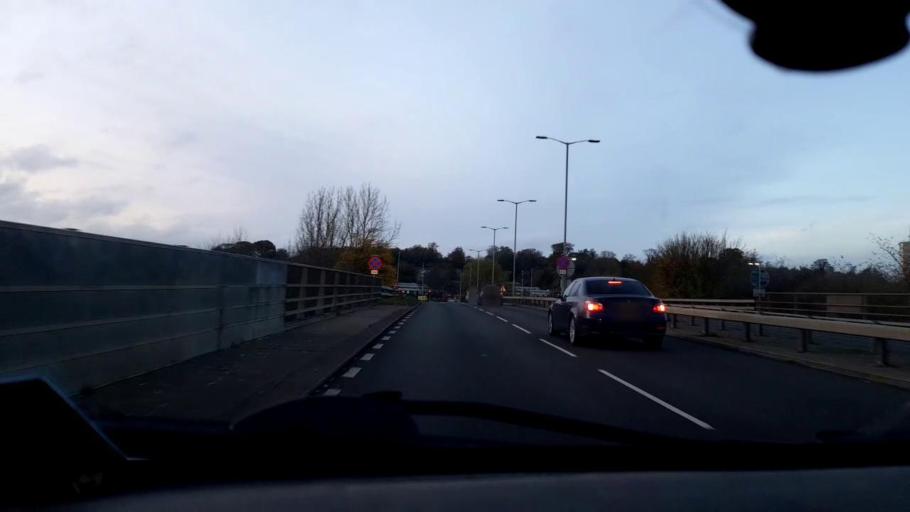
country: GB
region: England
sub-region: Norfolk
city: Thorpe Hamlet
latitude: 52.6107
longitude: 1.3088
